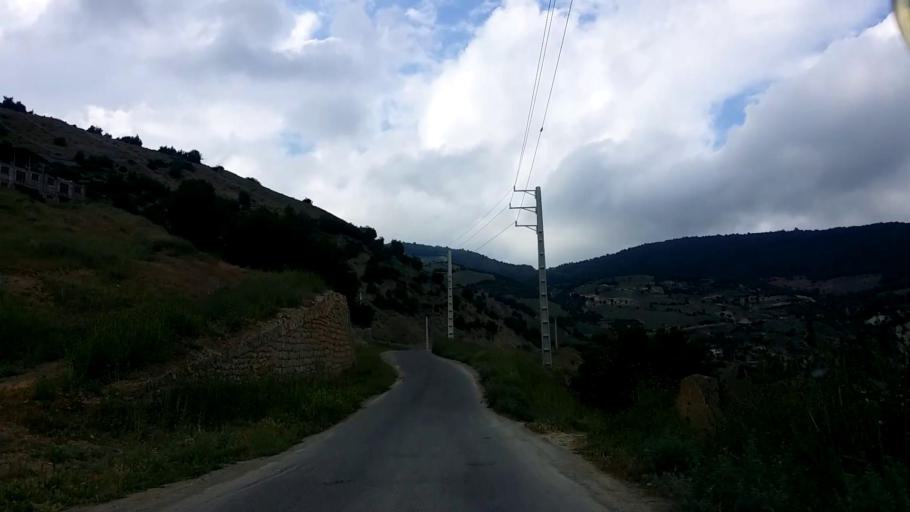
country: IR
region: Mazandaran
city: Chalus
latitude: 36.5460
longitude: 51.2712
